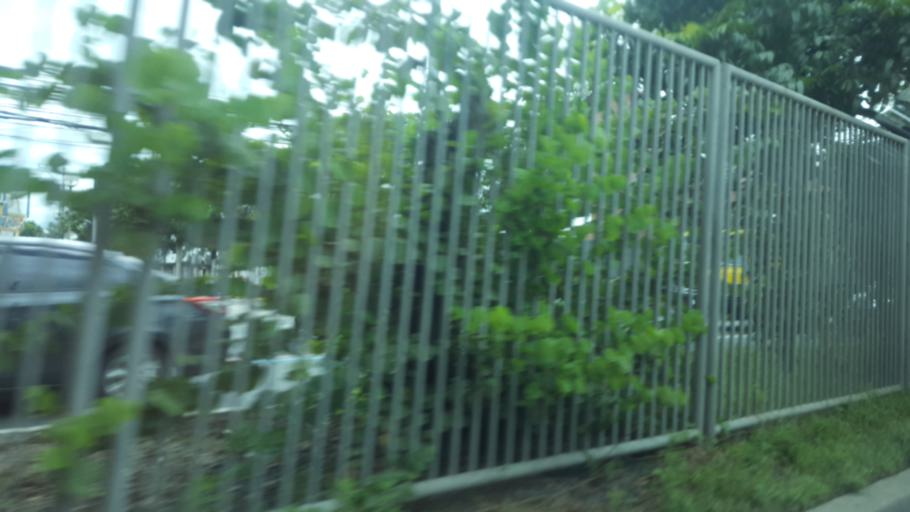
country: PH
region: Metro Manila
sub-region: Marikina
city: Calumpang
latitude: 14.6037
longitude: 121.0793
